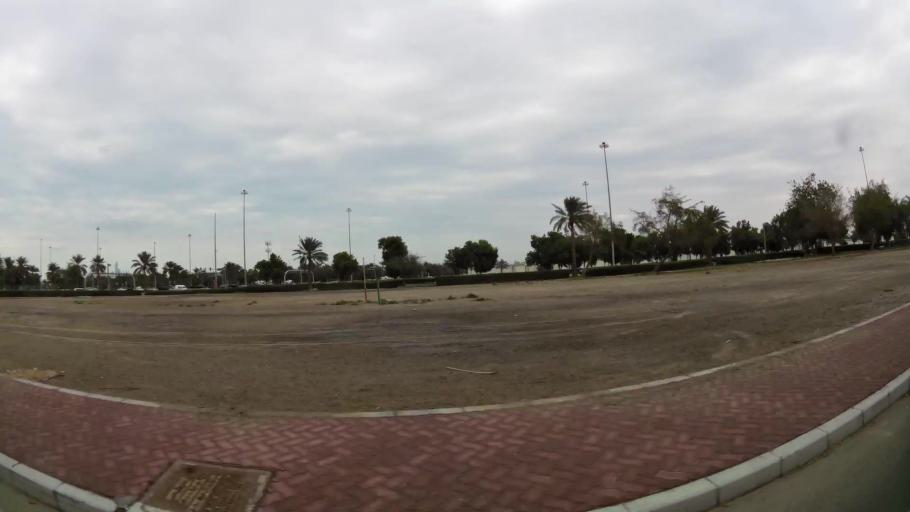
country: AE
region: Abu Dhabi
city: Abu Dhabi
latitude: 24.4329
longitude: 54.3770
